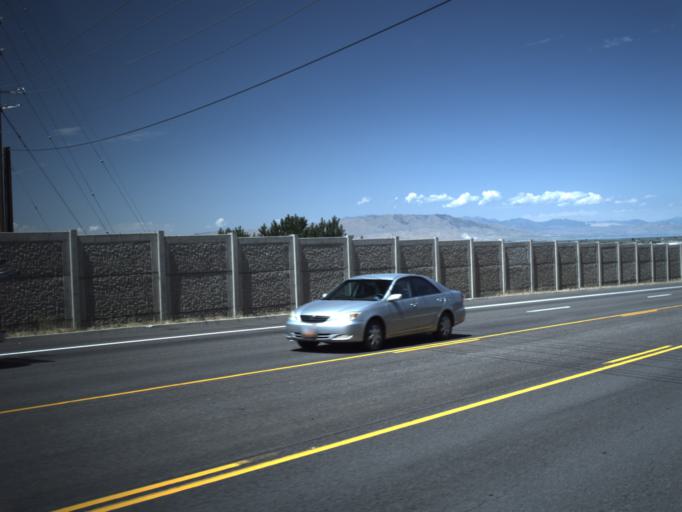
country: US
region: Utah
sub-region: Utah County
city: Spanish Fork
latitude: 40.1134
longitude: -111.6346
